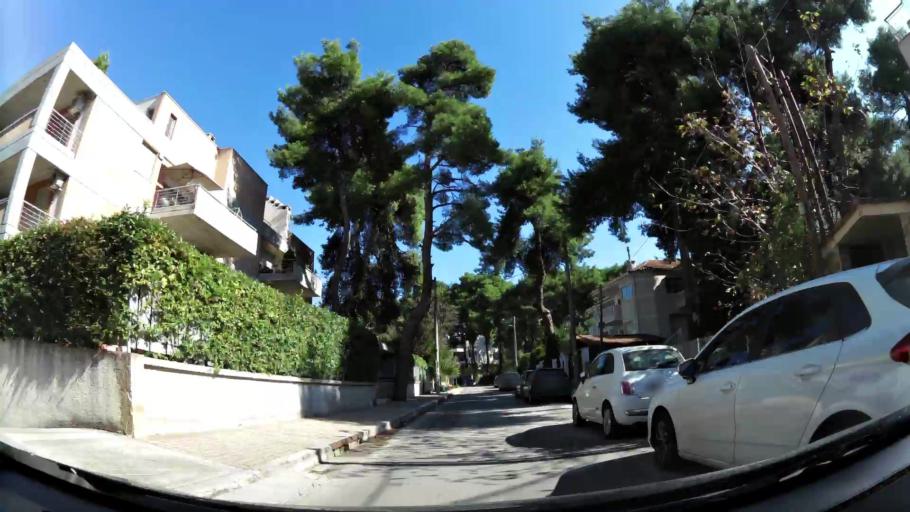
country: GR
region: Attica
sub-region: Nomarchia Anatolikis Attikis
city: Drosia
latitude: 38.1186
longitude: 23.8574
